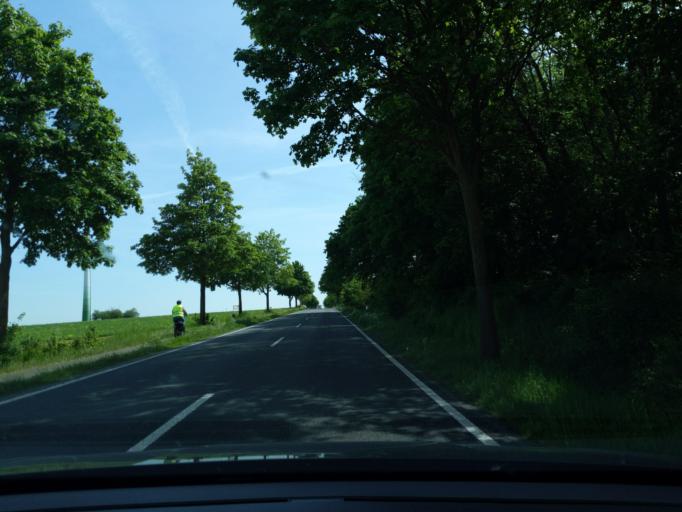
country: DE
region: Lower Saxony
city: Pattensen
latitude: 52.2147
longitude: 9.6805
